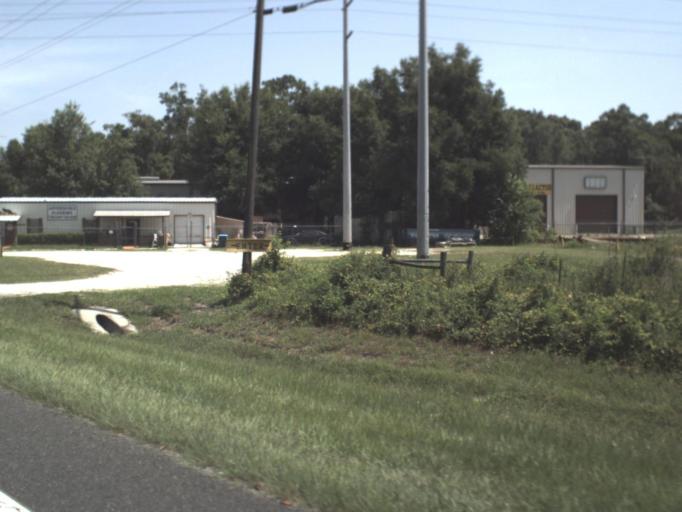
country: US
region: Florida
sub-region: Levy County
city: Manatee Road
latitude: 29.5255
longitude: -82.8846
